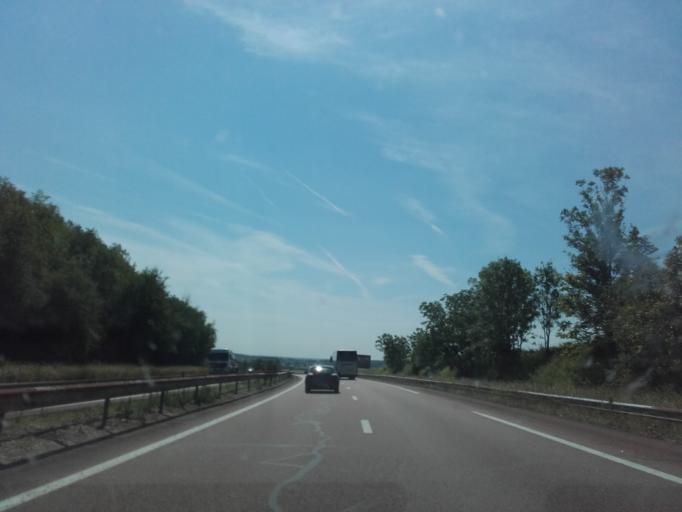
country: FR
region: Bourgogne
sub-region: Departement de l'Yonne
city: Avallon
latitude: 47.5541
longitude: 3.9528
